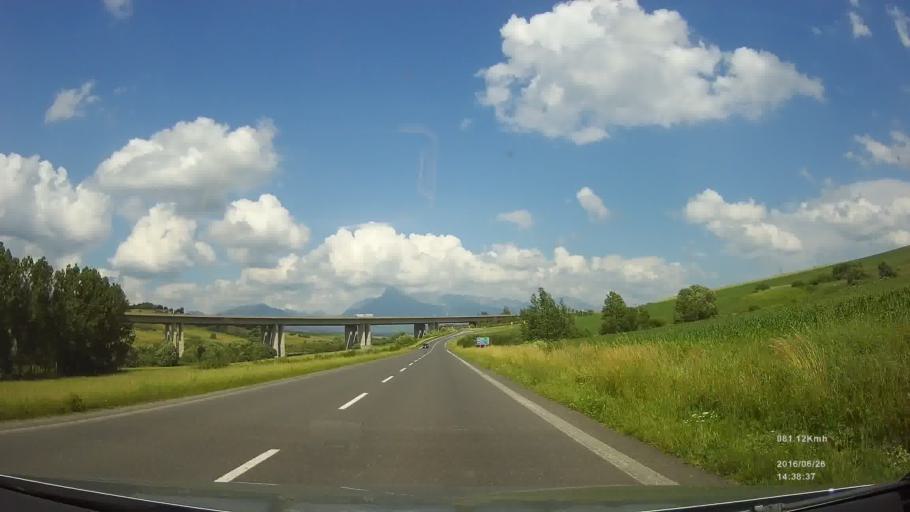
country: SK
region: Zilinsky
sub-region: Okres Liptovsky Mikulas
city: Hybe
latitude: 49.0527
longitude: 19.8437
